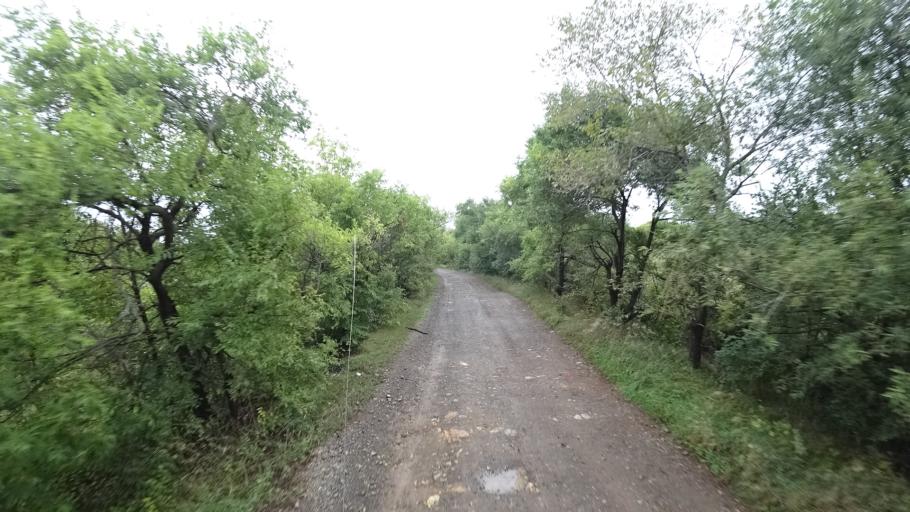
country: RU
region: Primorskiy
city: Monastyrishche
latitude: 44.2751
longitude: 132.4105
